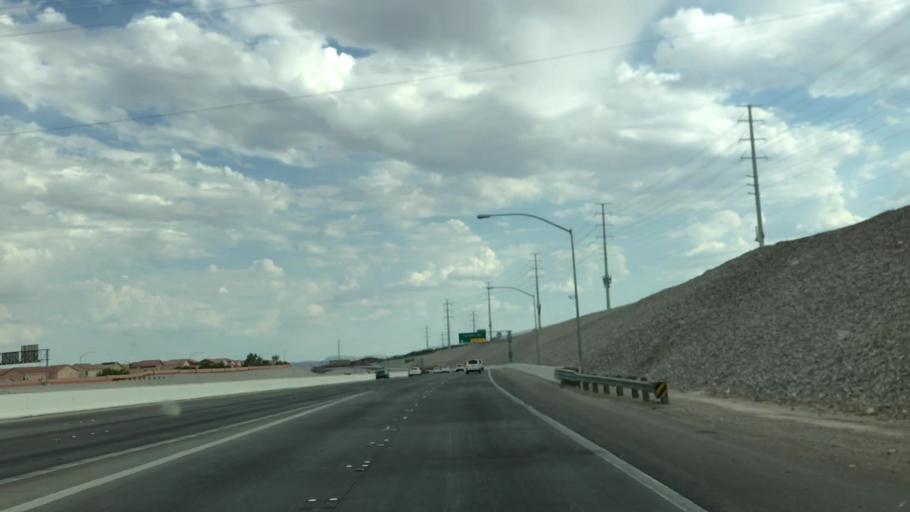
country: US
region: Nevada
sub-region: Clark County
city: Summerlin South
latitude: 36.1914
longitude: -115.3428
